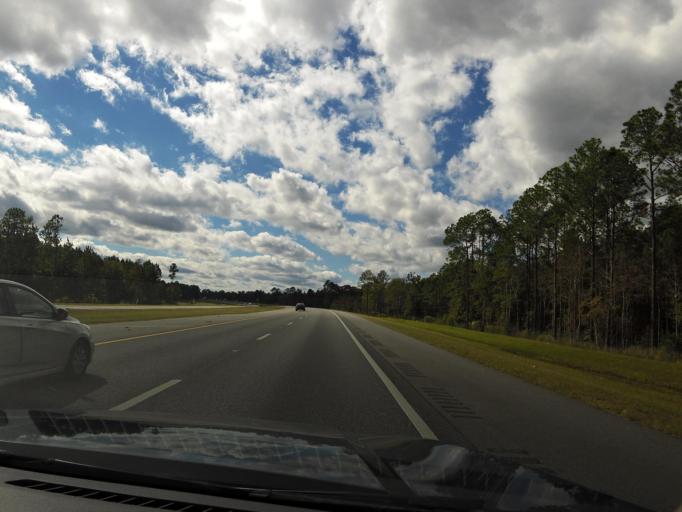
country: US
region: Florida
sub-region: Bradford County
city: Starke
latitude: 29.9861
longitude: -82.1094
